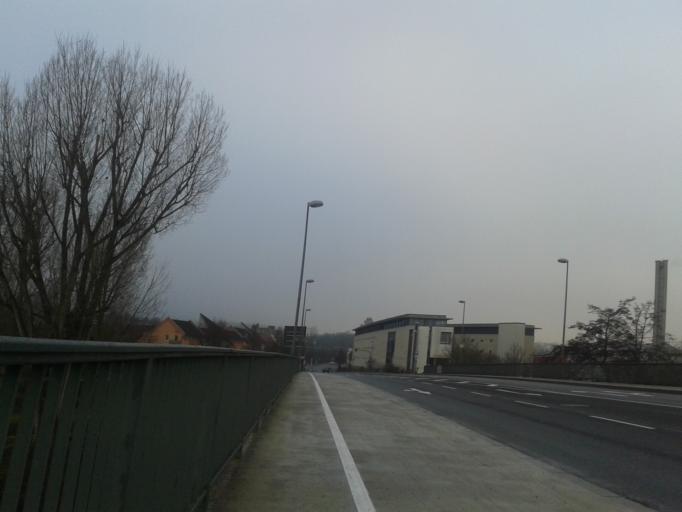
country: DE
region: Bavaria
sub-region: Upper Franconia
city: Bamberg
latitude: 49.9012
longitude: 10.8807
